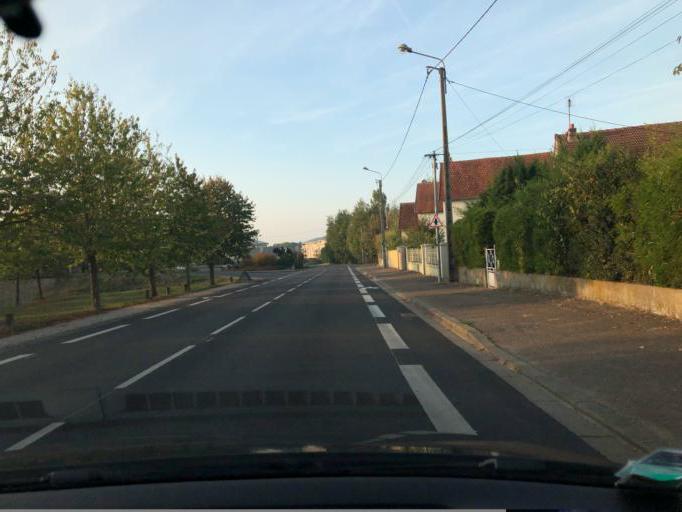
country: FR
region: Bourgogne
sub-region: Departement de l'Yonne
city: Sens
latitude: 48.2027
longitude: 3.2973
